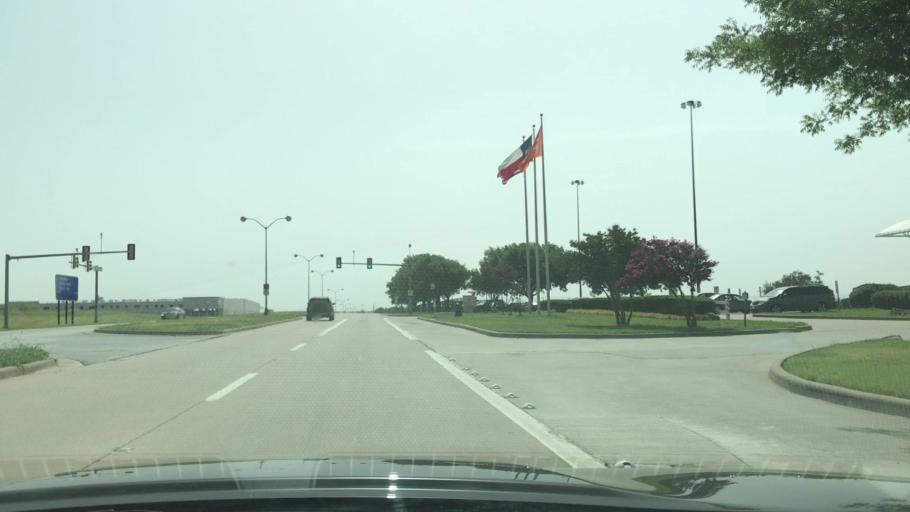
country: US
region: Texas
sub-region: Tarrant County
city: Euless
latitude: 32.8620
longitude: -97.0362
